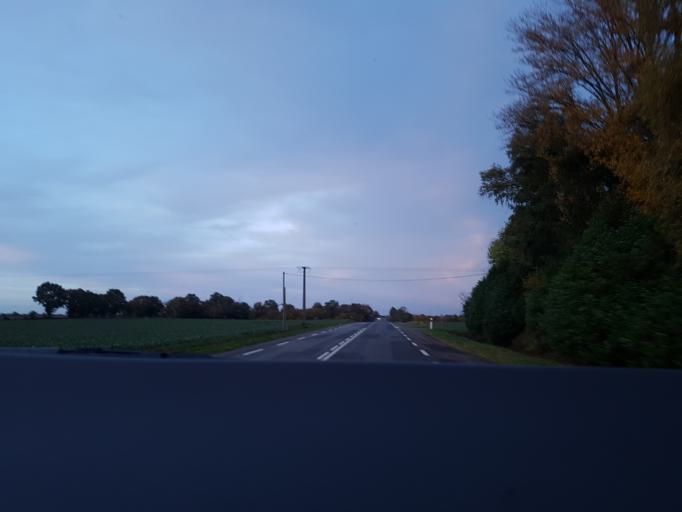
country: FR
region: Pays de la Loire
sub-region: Departement de la Mayenne
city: Cosse-le-Vivien
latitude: 47.9624
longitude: -0.8915
